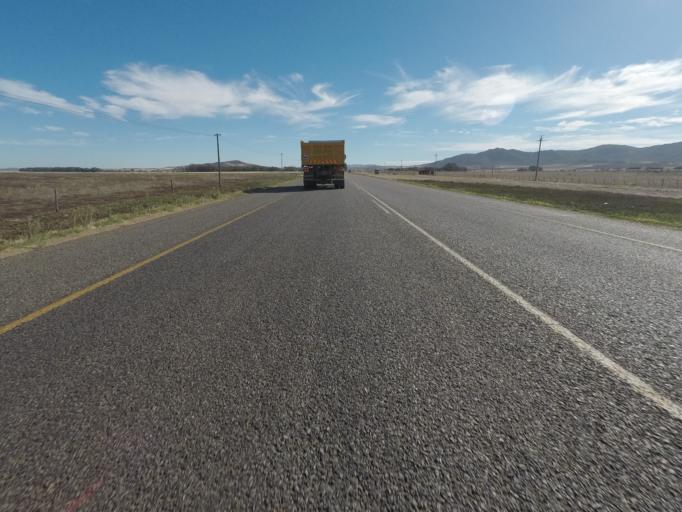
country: ZA
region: Western Cape
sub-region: West Coast District Municipality
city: Malmesbury
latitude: -33.6287
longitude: 18.7231
